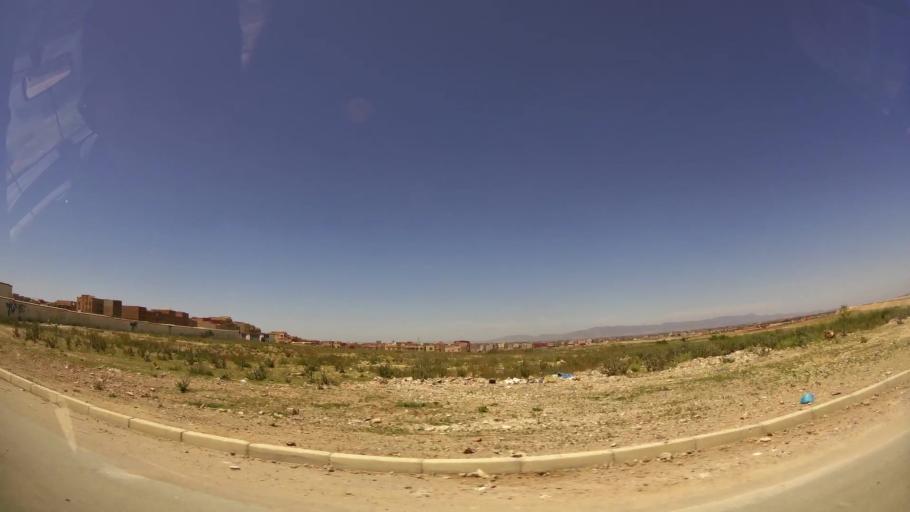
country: MA
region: Oriental
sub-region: Oujda-Angad
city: Oujda
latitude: 34.6871
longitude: -1.8681
